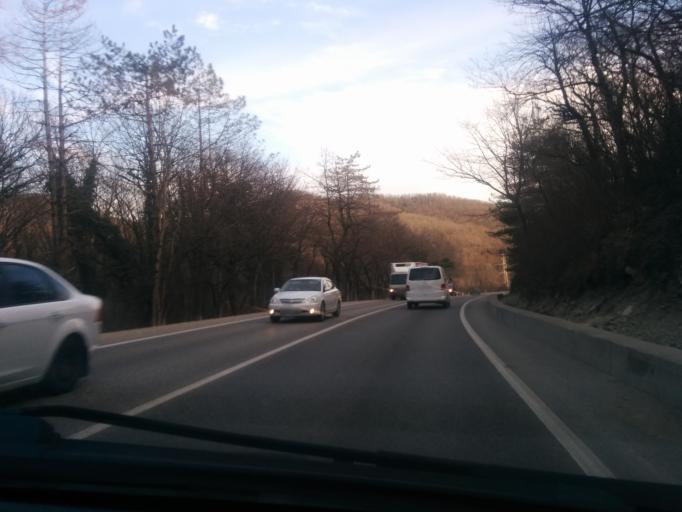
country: RU
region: Krasnodarskiy
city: Ol'ginka
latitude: 44.2389
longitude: 38.8972
